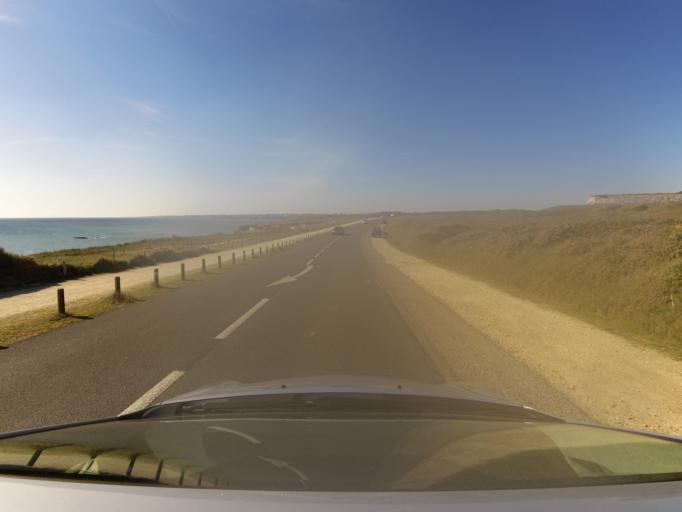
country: FR
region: Brittany
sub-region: Departement du Morbihan
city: Guidel-Plage
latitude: 47.7497
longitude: -3.5093
